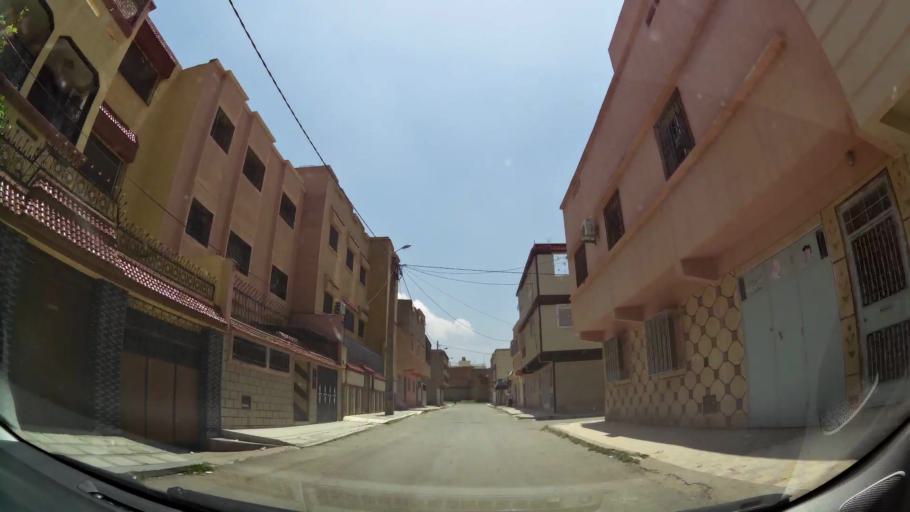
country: MA
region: Oriental
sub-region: Oujda-Angad
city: Oujda
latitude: 34.6820
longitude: -1.8907
